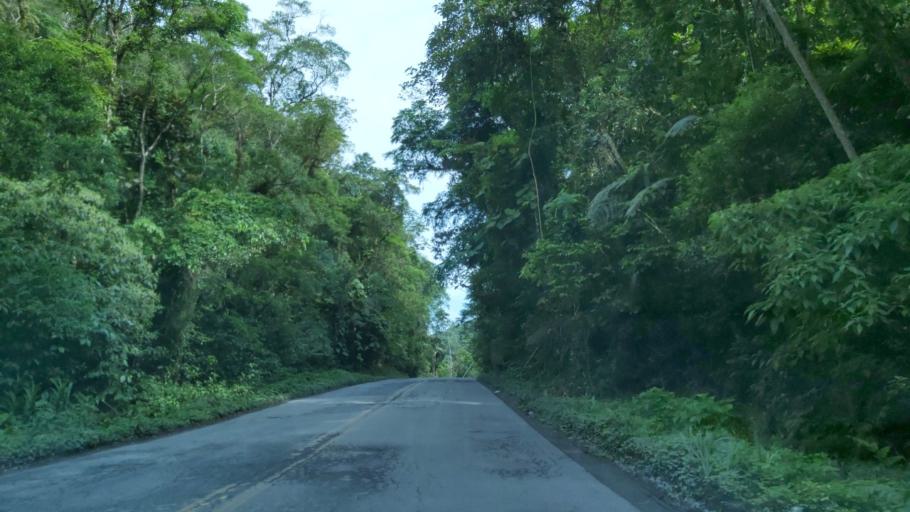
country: BR
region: Sao Paulo
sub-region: Miracatu
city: Miracatu
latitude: -24.0317
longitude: -47.5580
